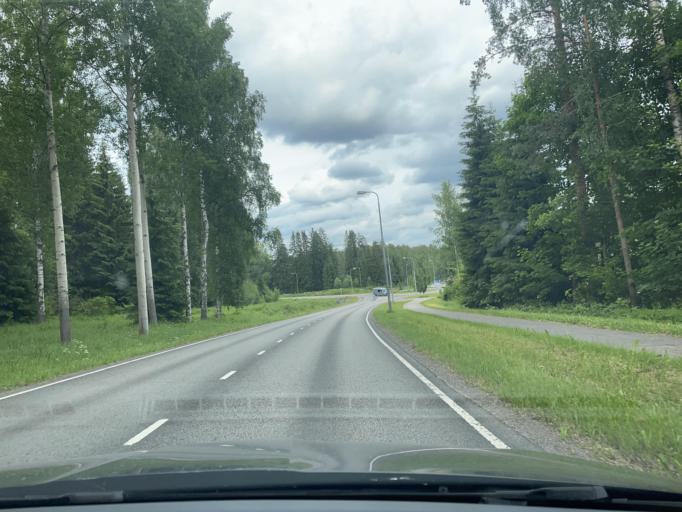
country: FI
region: Central Finland
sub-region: Jaemsae
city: Jaemsaenkoski
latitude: 61.9218
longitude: 25.1541
